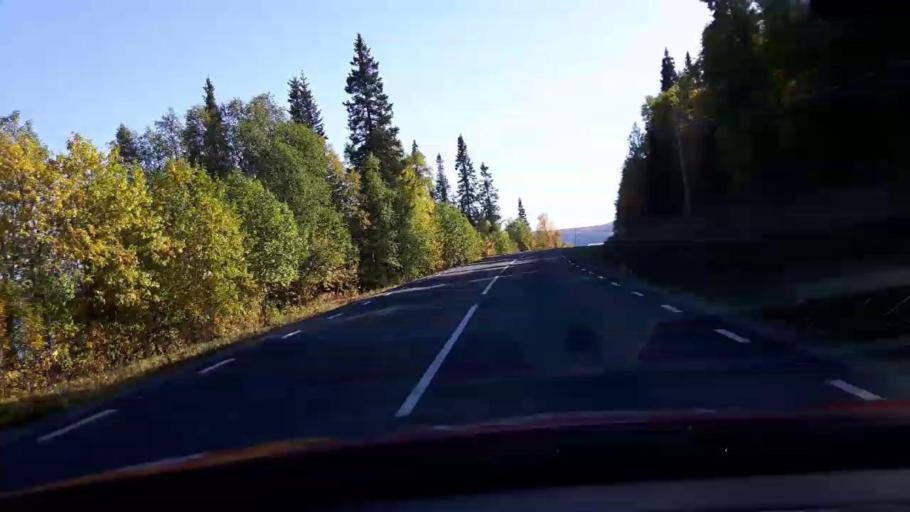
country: NO
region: Nord-Trondelag
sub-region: Royrvik
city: Royrvik
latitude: 64.8317
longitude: 14.0782
